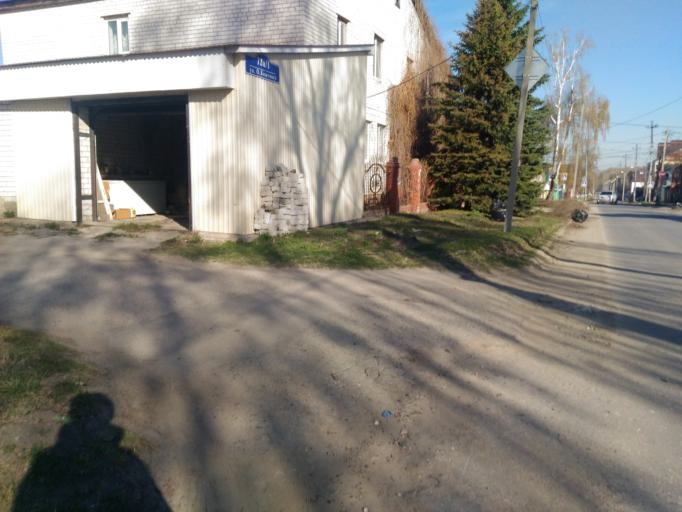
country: RU
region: Ulyanovsk
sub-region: Ulyanovskiy Rayon
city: Ulyanovsk
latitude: 54.3509
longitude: 48.3764
